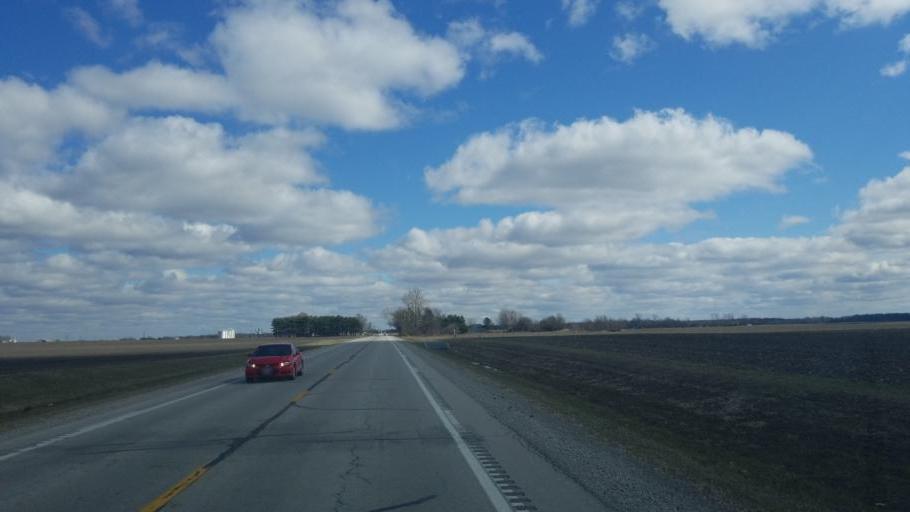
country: US
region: Illinois
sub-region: Douglas County
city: Villa Grove
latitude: 39.7921
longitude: -88.0415
